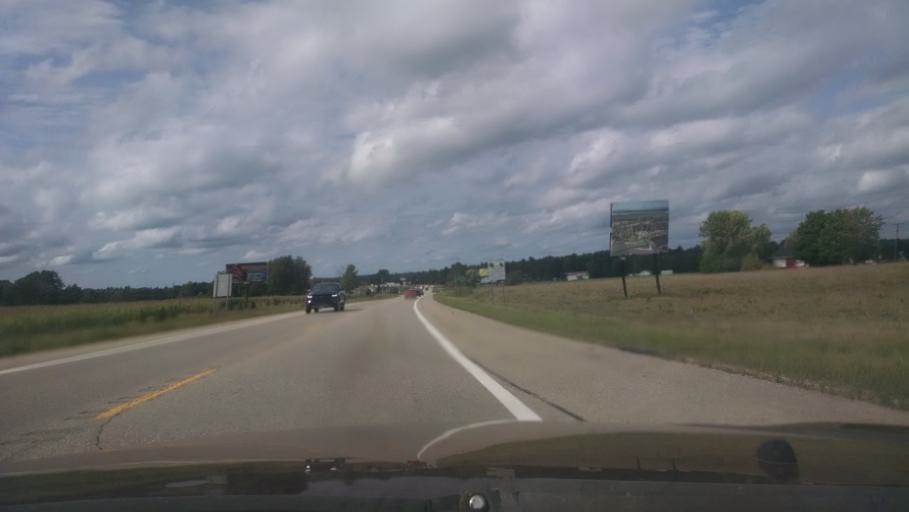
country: US
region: Michigan
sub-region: Wexford County
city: Cadillac
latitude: 44.2206
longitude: -85.4365
